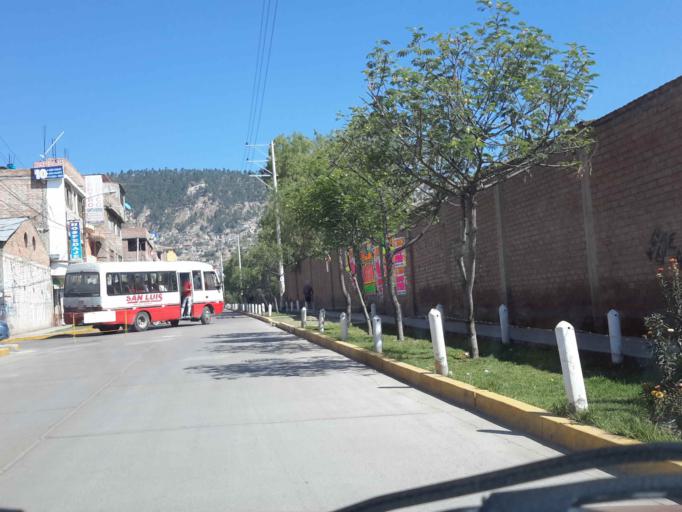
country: PE
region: Ayacucho
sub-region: Provincia de Huamanga
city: Ayacucho
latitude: -13.1556
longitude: -74.2213
